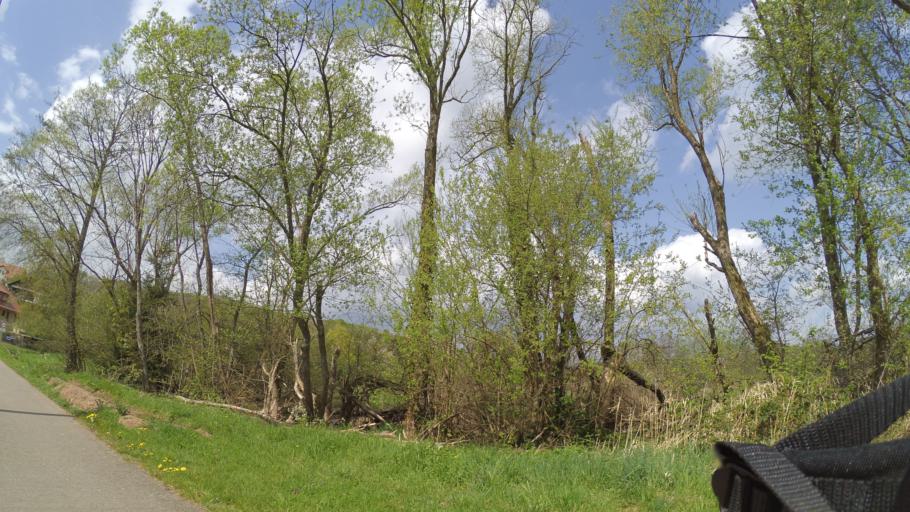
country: DE
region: Saarland
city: Wadern
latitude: 49.5711
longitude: 6.9262
